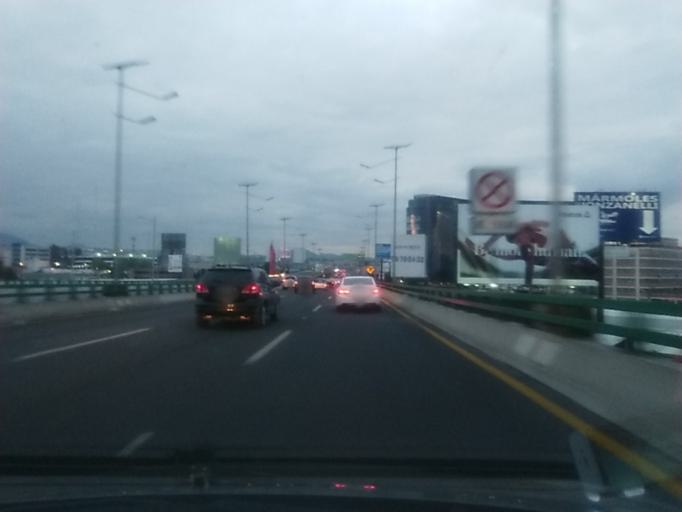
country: MX
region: Mexico
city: Naucalpan de Juarez
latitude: 19.4756
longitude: -99.2297
